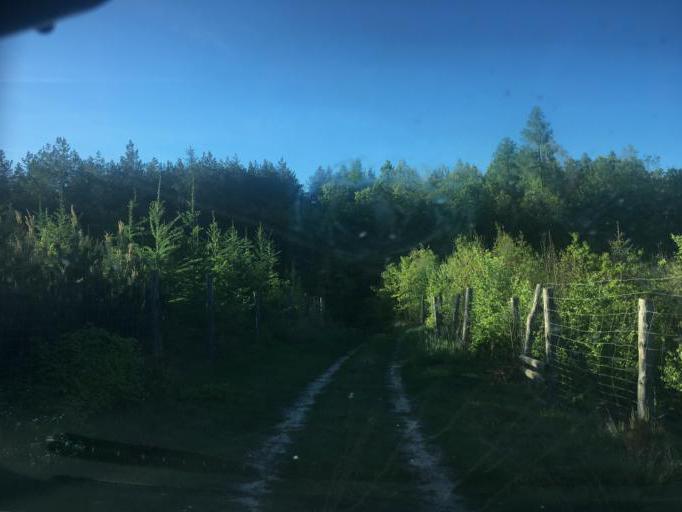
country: PL
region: Kujawsko-Pomorskie
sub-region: Powiat brodnicki
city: Gorzno
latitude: 53.2189
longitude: 19.7210
